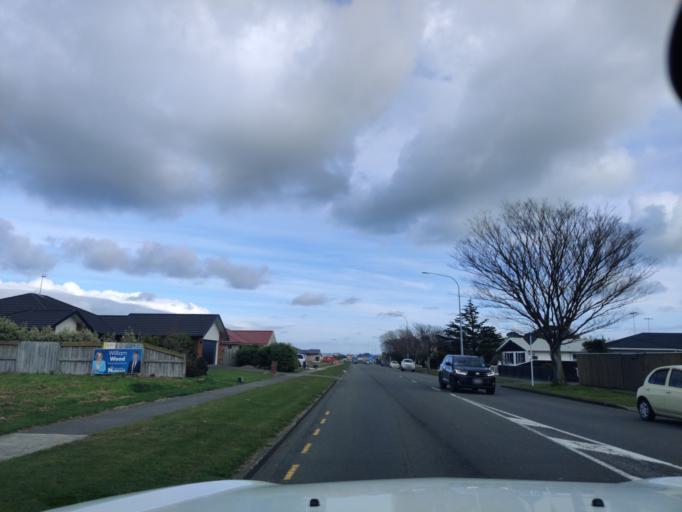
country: NZ
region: Manawatu-Wanganui
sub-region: Palmerston North City
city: Palmerston North
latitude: -40.3364
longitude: 175.6062
